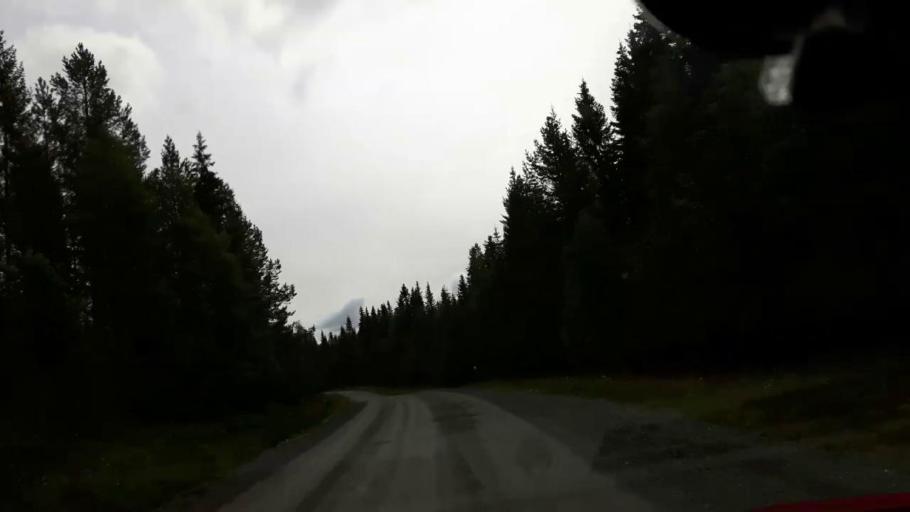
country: SE
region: Jaemtland
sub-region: Krokoms Kommun
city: Valla
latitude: 63.6625
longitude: 13.9684
